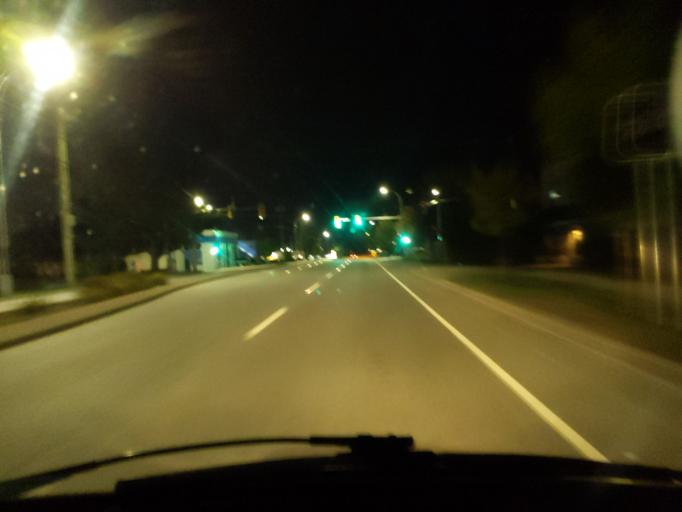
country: CA
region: British Columbia
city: Pitt Meadows
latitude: 49.1741
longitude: -122.6907
